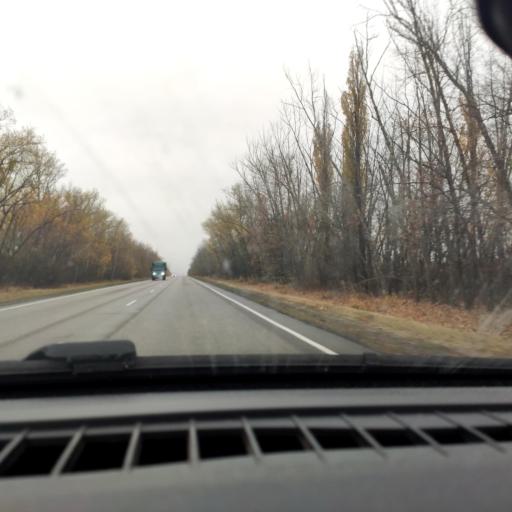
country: RU
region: Voronezj
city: Ostrogozhsk
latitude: 51.0112
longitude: 38.9932
